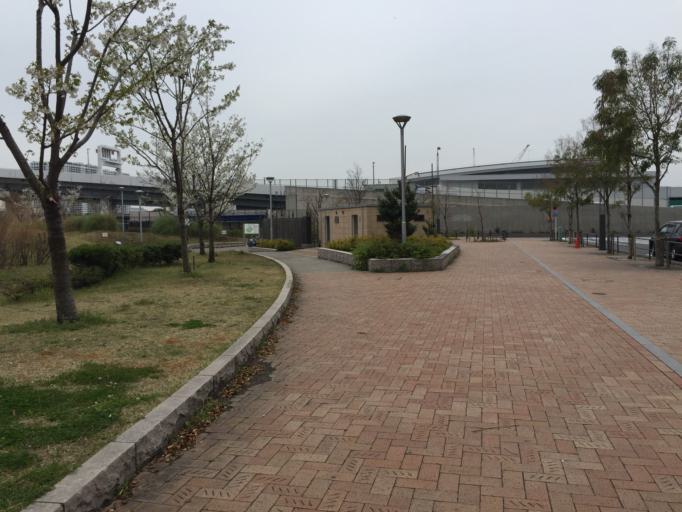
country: JP
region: Tokyo
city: Urayasu
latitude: 35.6469
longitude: 139.7912
